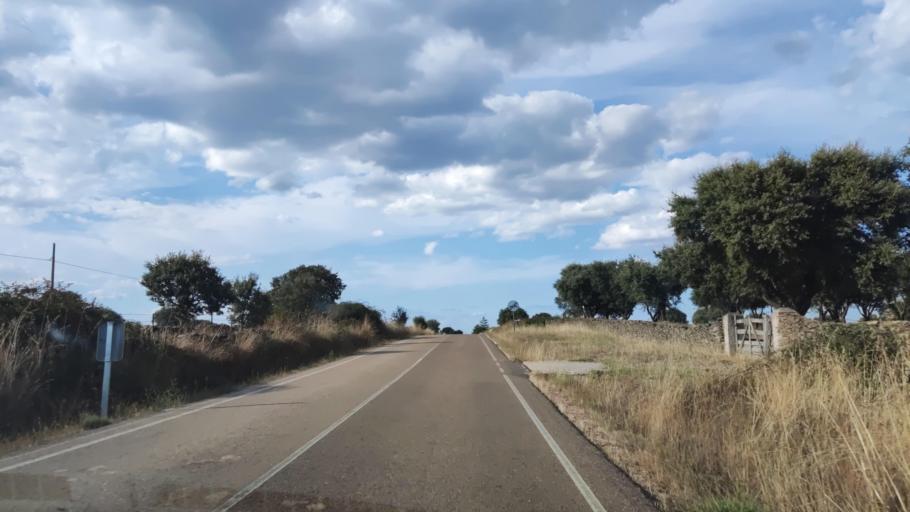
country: ES
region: Castille and Leon
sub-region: Provincia de Salamanca
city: Martiago
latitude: 40.4587
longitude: -6.4901
